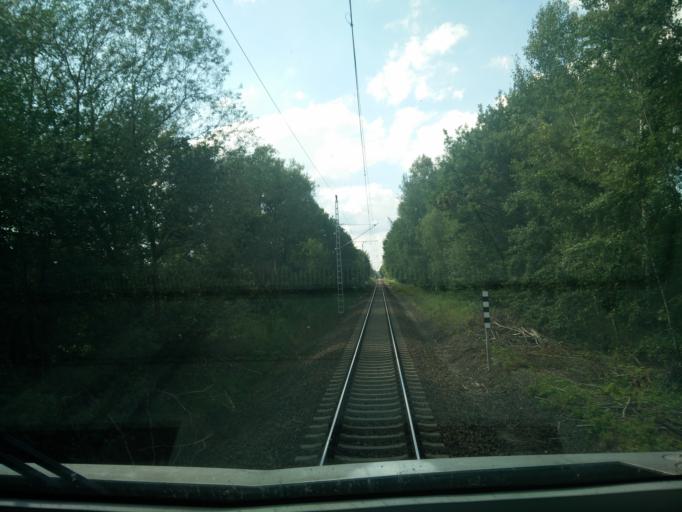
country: DE
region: Brandenburg
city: Werben
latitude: 51.7714
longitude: 14.1758
